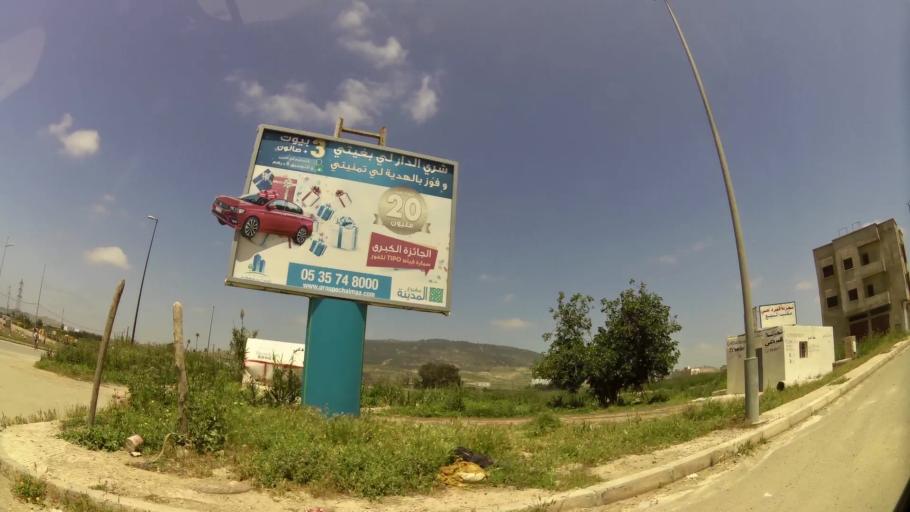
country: MA
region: Fes-Boulemane
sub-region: Fes
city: Fes
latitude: 34.0350
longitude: -5.0598
